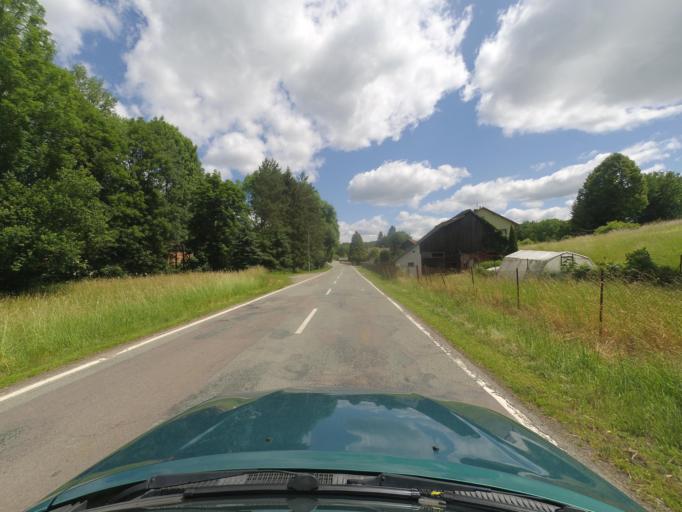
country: CZ
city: Dobruska
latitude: 50.3233
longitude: 16.2082
